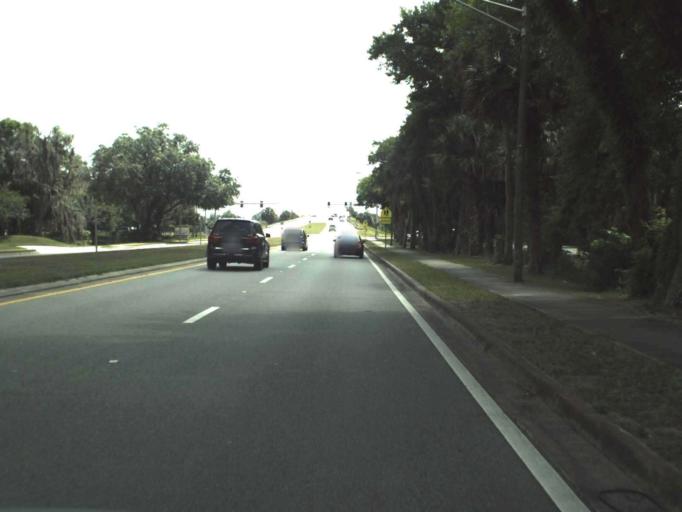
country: US
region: Florida
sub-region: Volusia County
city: New Smyrna Beach
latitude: 29.0187
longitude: -80.9307
